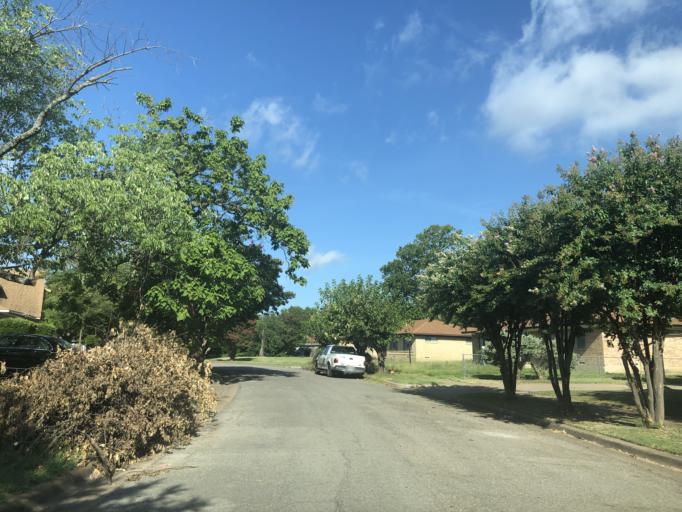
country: US
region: Texas
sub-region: Dallas County
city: Duncanville
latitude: 32.6587
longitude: -96.9105
